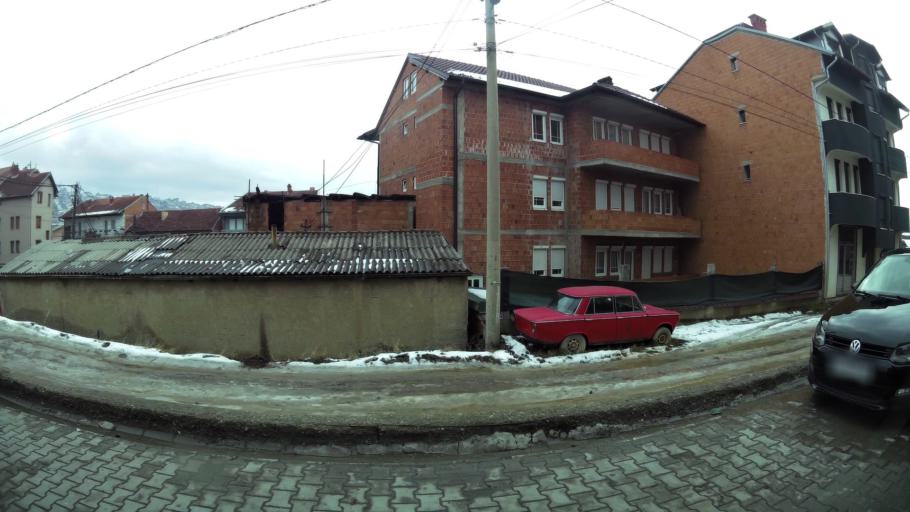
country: XK
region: Pristina
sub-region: Komuna e Prishtines
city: Pristina
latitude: 42.6738
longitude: 21.1658
